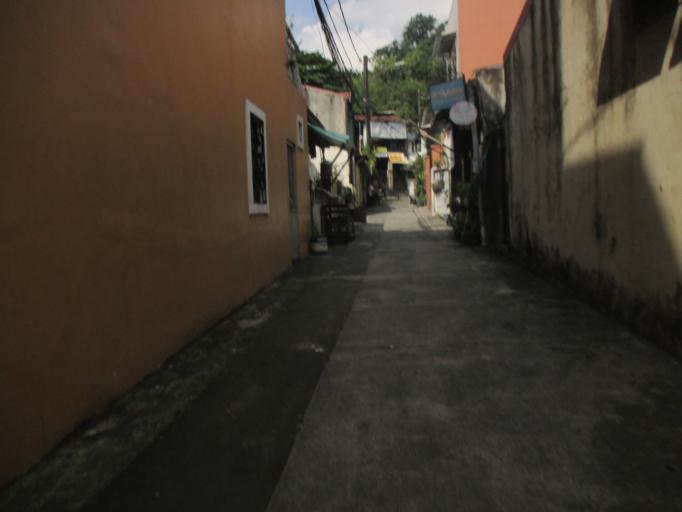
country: PH
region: Metro Manila
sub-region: Marikina
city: Calumpang
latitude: 14.6358
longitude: 121.0822
